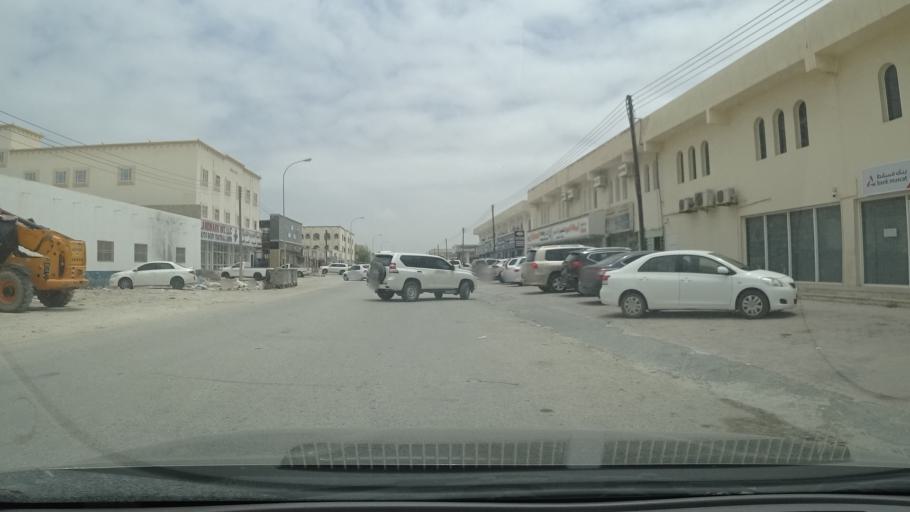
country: OM
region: Zufar
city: Salalah
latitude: 17.0217
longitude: 54.0511
